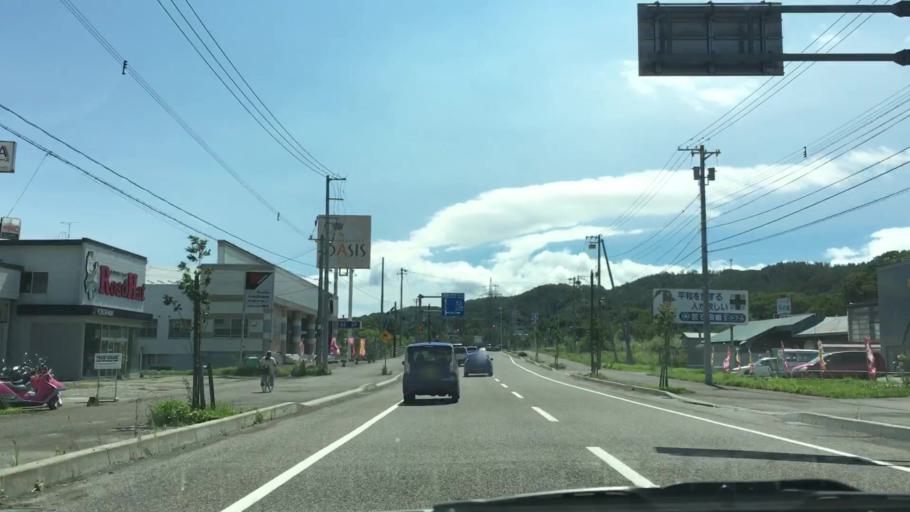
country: JP
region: Hokkaido
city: Otofuke
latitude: 43.2342
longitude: 143.5462
